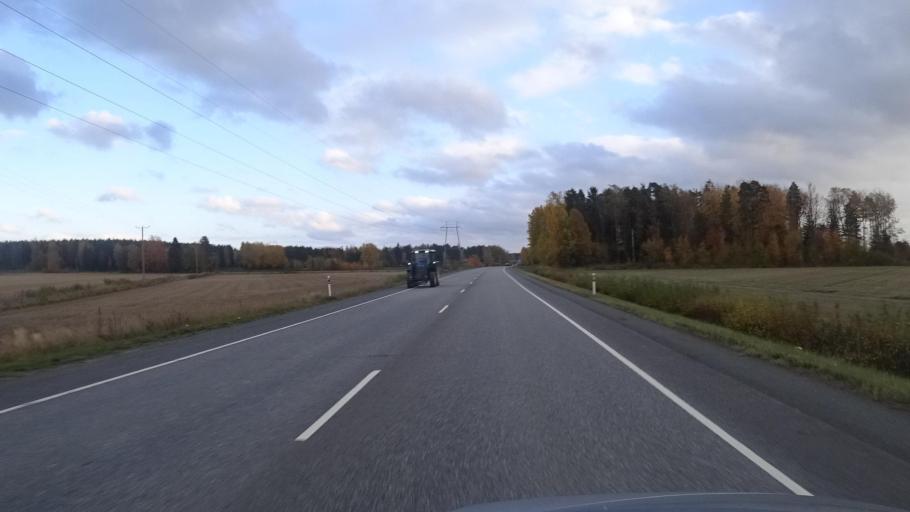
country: FI
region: Satakunta
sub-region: Rauma
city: Saekylae
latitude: 61.0268
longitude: 22.4013
